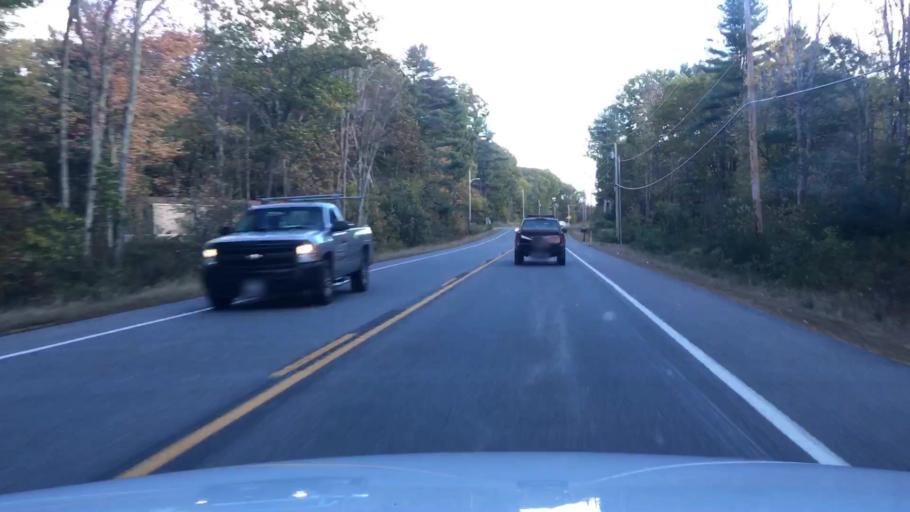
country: US
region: Maine
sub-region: York County
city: Wells Beach Station
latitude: 43.3412
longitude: -70.6387
